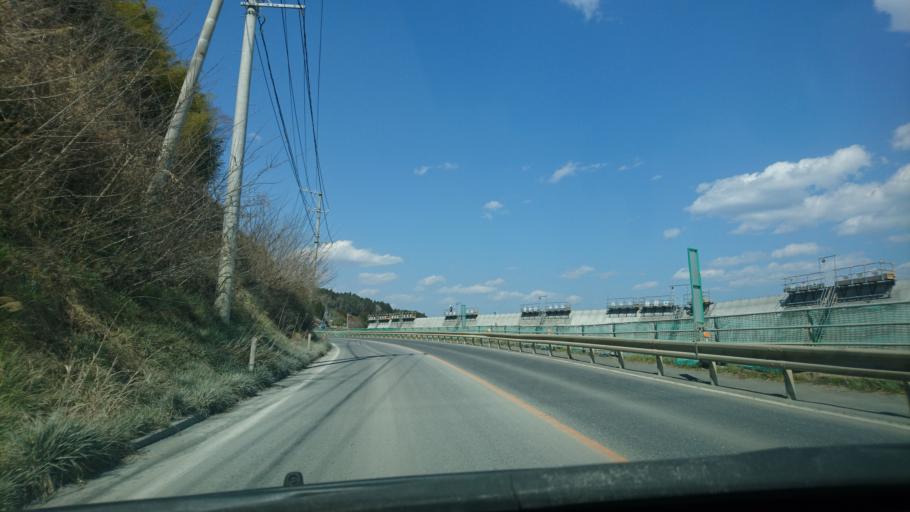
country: JP
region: Miyagi
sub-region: Oshika Gun
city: Onagawa Cho
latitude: 38.6491
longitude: 141.4428
